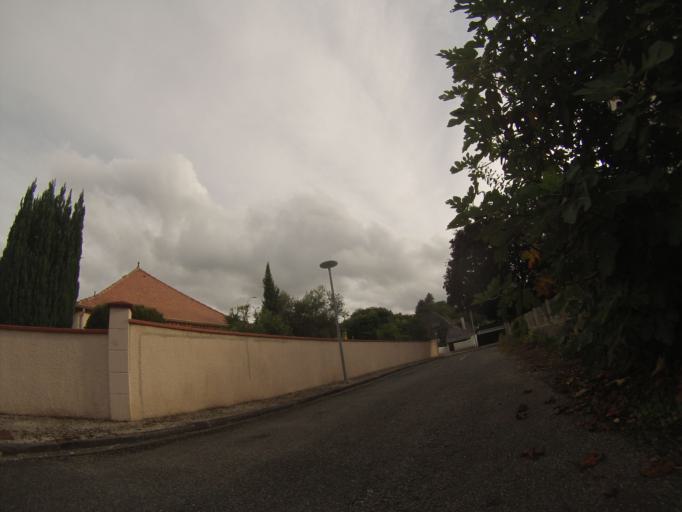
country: FR
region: Aquitaine
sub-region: Departement des Pyrenees-Atlantiques
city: Gelos
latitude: 43.2810
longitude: -0.3727
